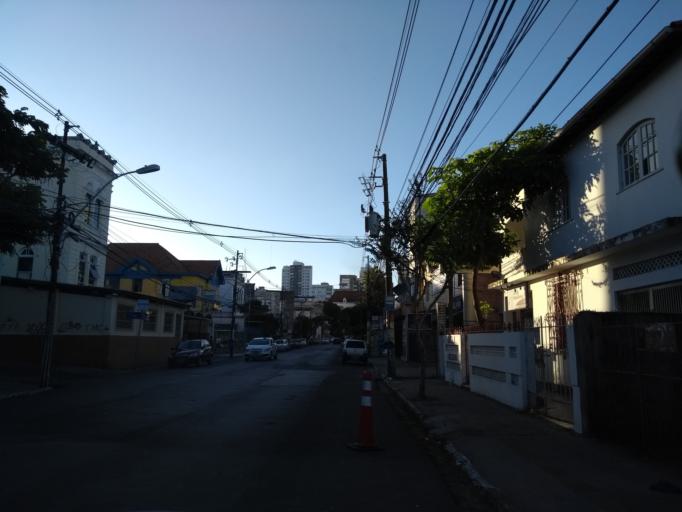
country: BR
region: Bahia
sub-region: Salvador
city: Salvador
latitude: -12.9920
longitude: -38.5166
